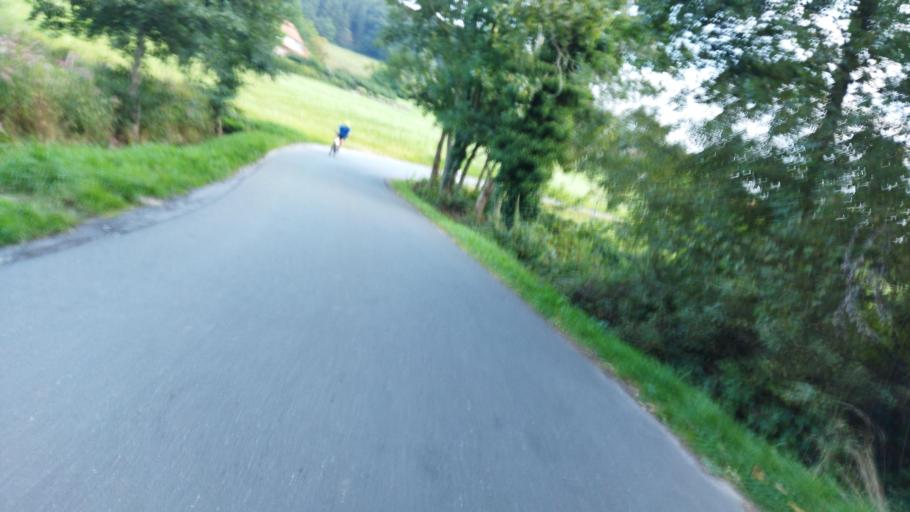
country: DE
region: Lower Saxony
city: Hagen
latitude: 52.1945
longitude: 8.0080
